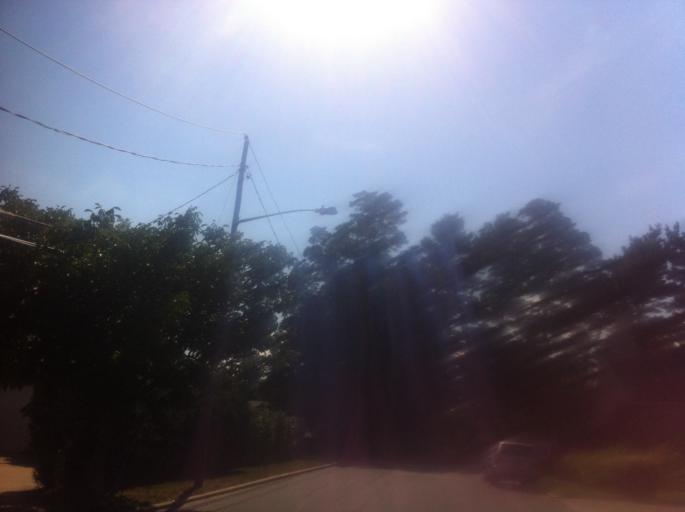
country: US
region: New York
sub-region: Nassau County
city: Glen Cove
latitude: 40.8590
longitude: -73.6120
